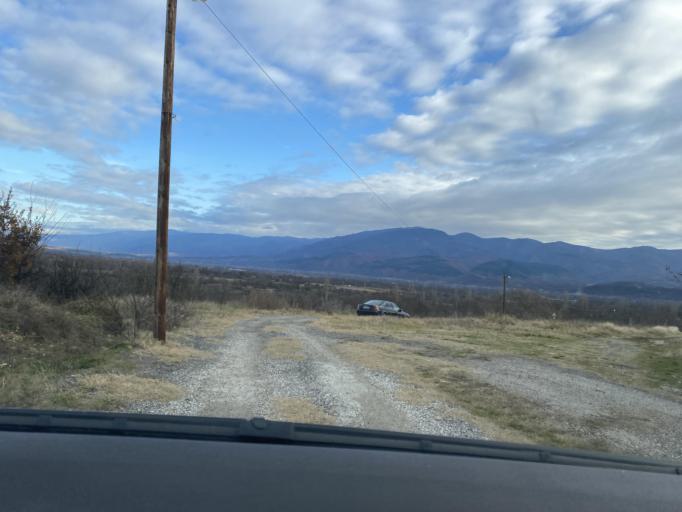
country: MK
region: Opstina Rankovce
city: Rankovce
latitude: 42.1846
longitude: 22.1094
